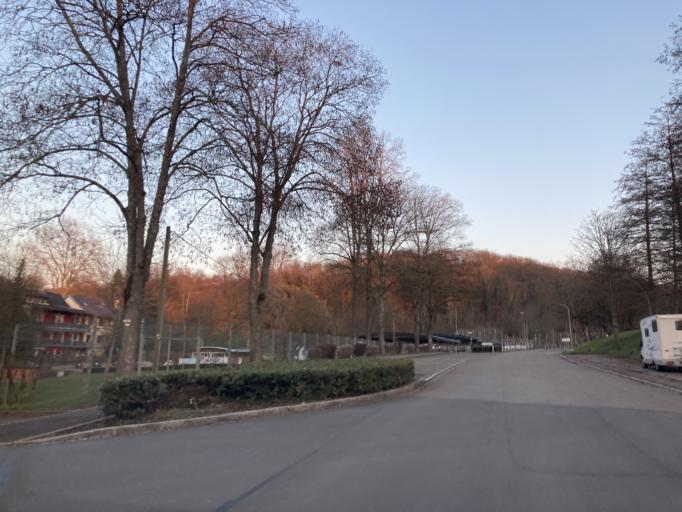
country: DE
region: Baden-Wuerttemberg
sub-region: Freiburg Region
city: Mullheim
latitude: 47.8029
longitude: 7.6329
